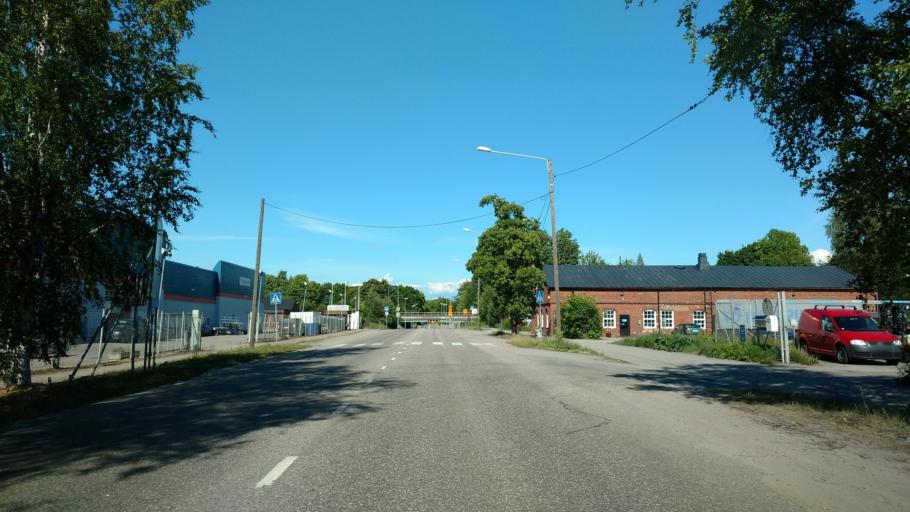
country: FI
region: Varsinais-Suomi
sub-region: Salo
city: Salo
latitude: 60.3805
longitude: 23.1229
